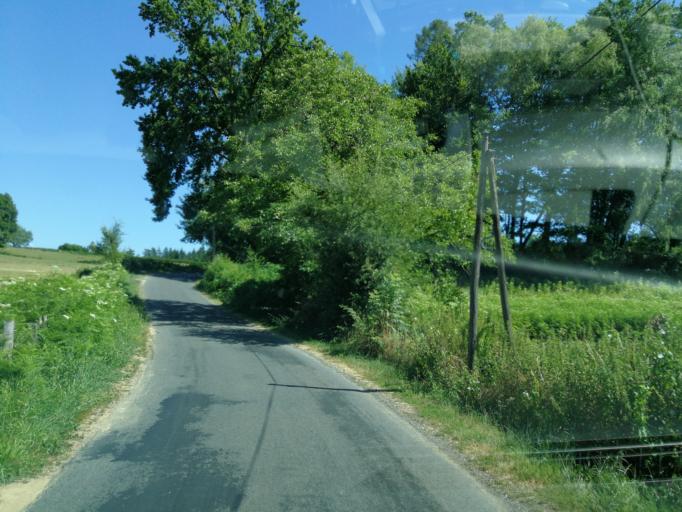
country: FR
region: Limousin
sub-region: Departement de la Correze
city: Sainte-Fereole
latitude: 45.2339
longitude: 1.5939
